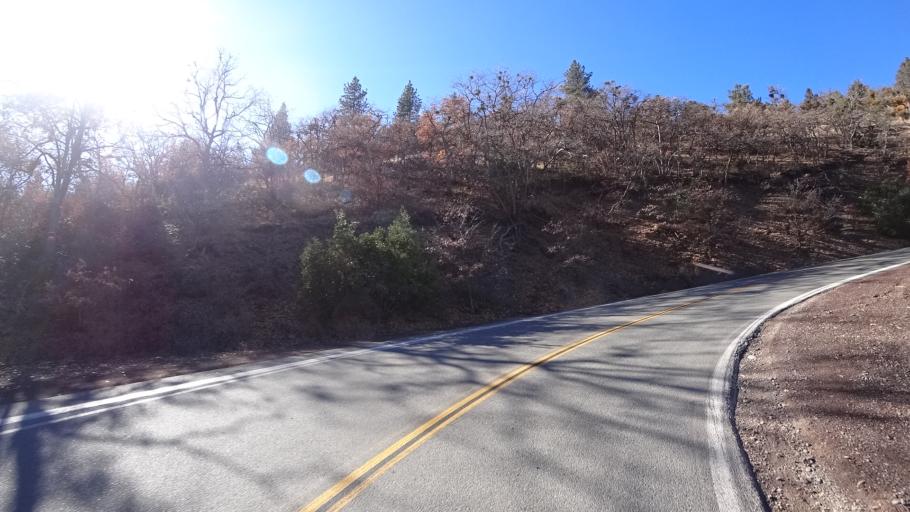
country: US
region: California
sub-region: Siskiyou County
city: Weed
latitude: 41.4476
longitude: -122.6410
